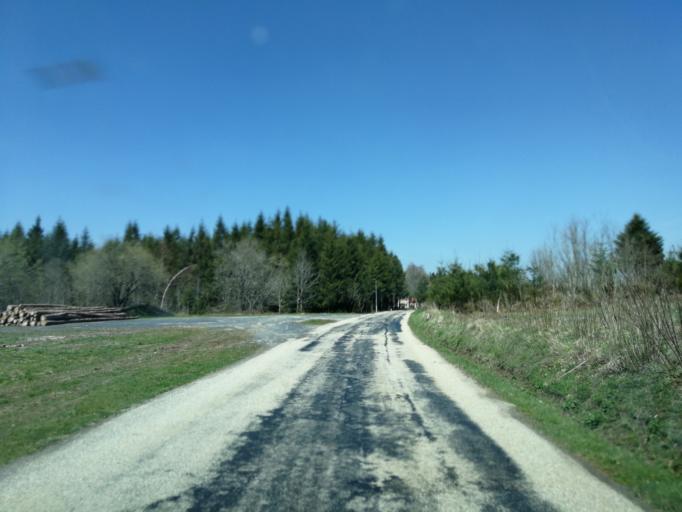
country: FR
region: Auvergne
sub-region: Departement de la Haute-Loire
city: Montfaucon-en-Velay
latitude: 45.1301
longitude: 4.3964
